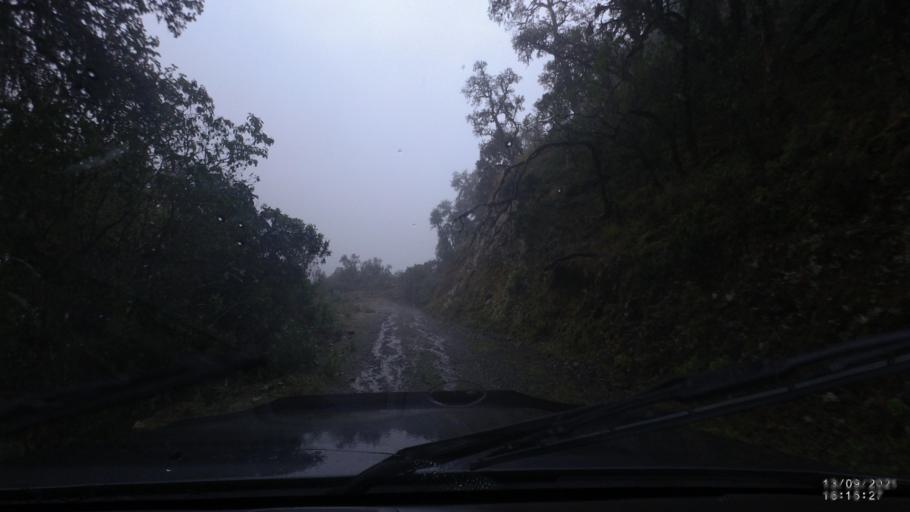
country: BO
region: Cochabamba
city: Colomi
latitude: -17.2746
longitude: -65.7112
